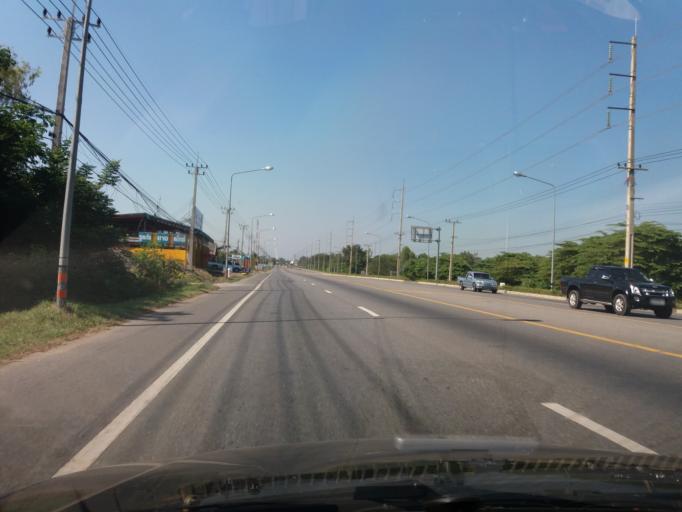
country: TH
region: Chai Nat
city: Wat Sing
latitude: 15.2540
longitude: 100.0963
